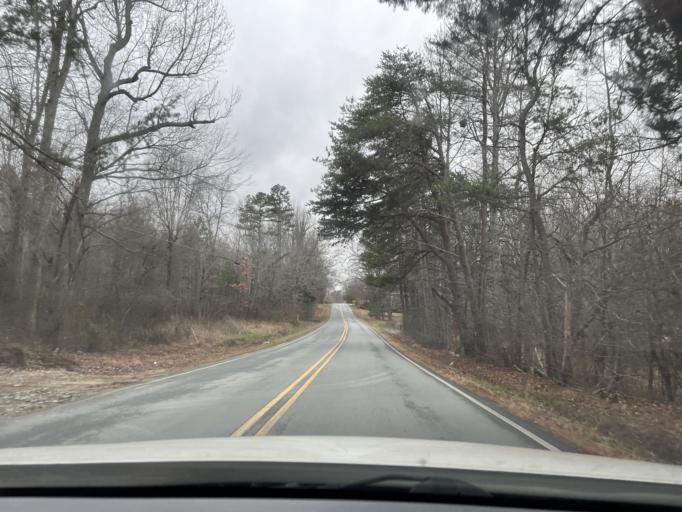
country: US
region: North Carolina
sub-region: Guilford County
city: Pleasant Garden
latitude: 35.9937
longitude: -79.8003
